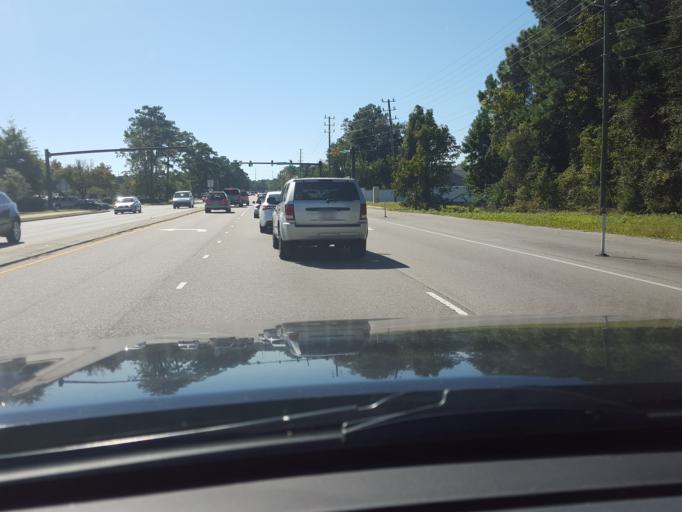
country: US
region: North Carolina
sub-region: New Hanover County
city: Seagate
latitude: 34.2328
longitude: -77.8290
